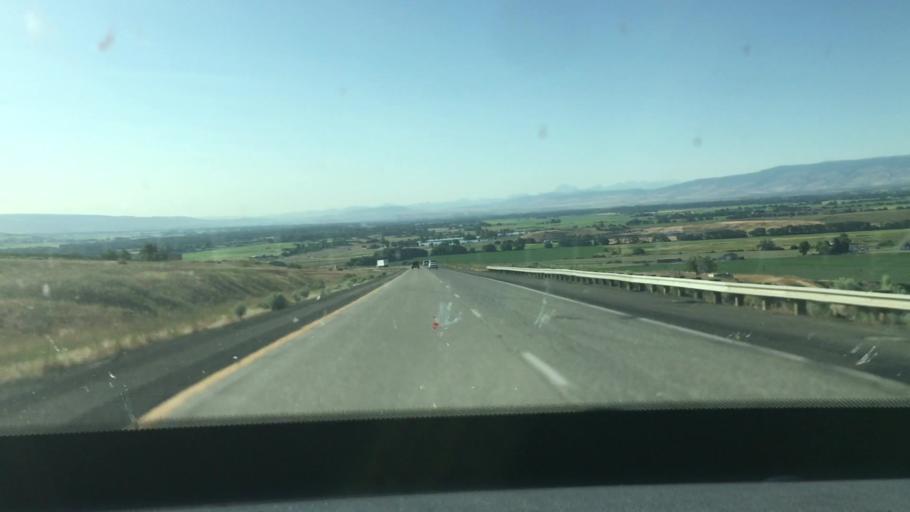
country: US
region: Washington
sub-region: Kittitas County
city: Kittitas
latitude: 46.9214
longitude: -120.4853
